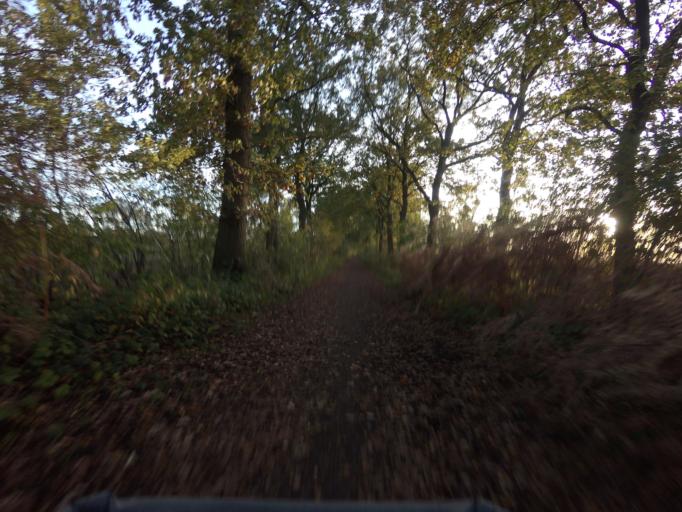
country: NL
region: Utrecht
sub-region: Gemeente De Bilt
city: De Bilt
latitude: 52.1472
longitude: 5.1775
